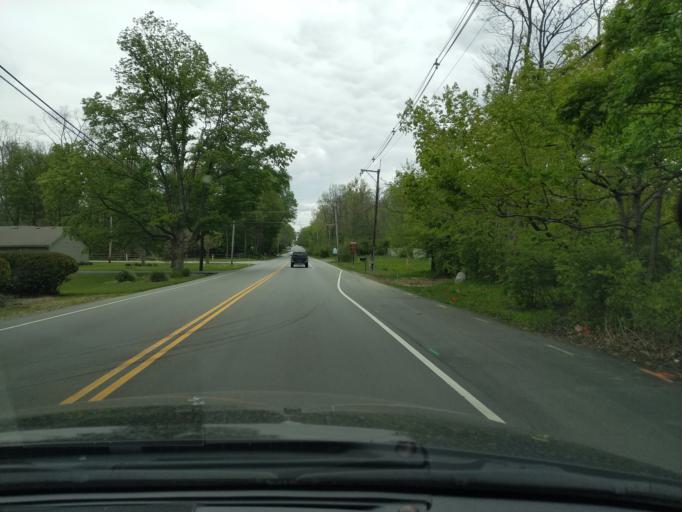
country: US
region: Indiana
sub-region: Hamilton County
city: Carmel
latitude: 39.9480
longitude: -86.1268
